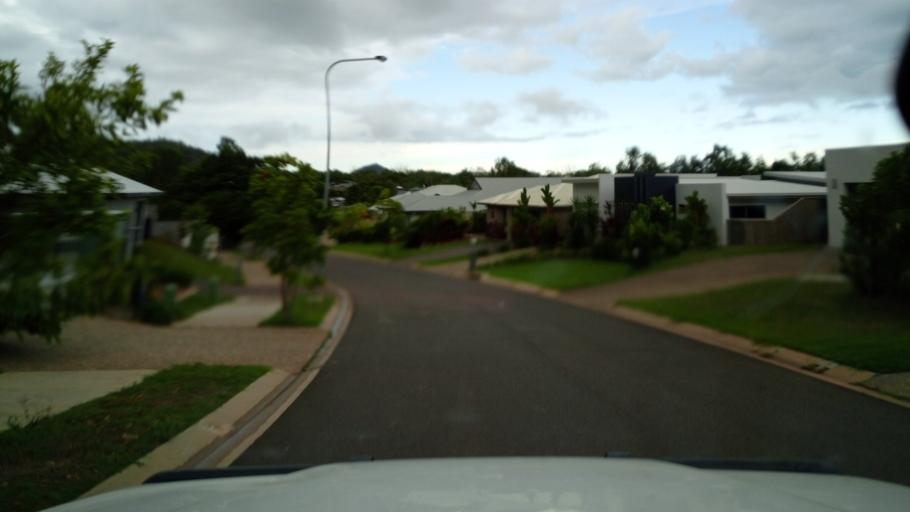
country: AU
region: Queensland
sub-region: Cairns
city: Redlynch
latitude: -16.8440
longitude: 145.6884
